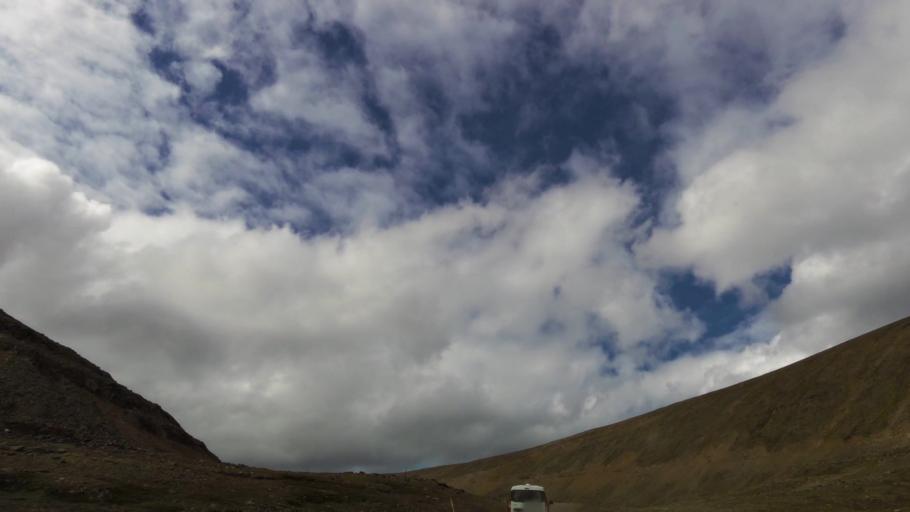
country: IS
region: Westfjords
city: Isafjoerdur
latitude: 66.1710
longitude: -23.3527
